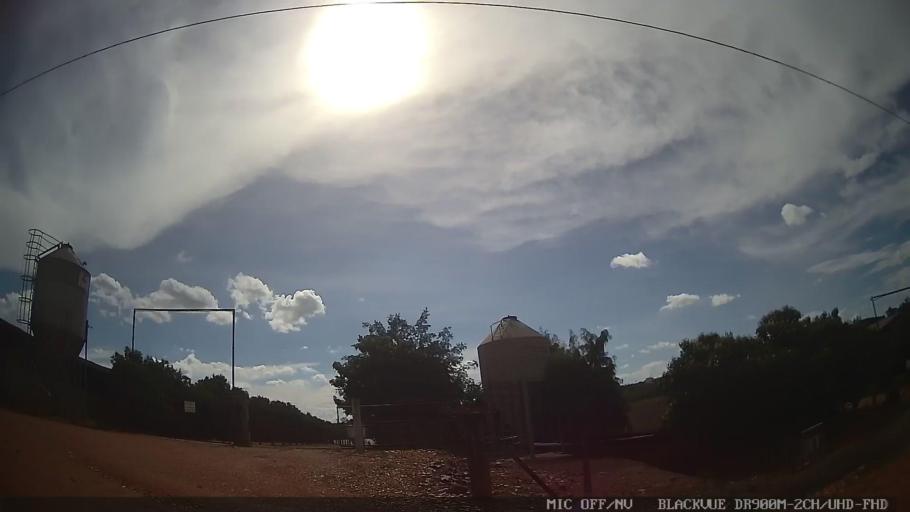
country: BR
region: Sao Paulo
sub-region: Conchas
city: Conchas
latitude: -23.0303
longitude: -47.9955
